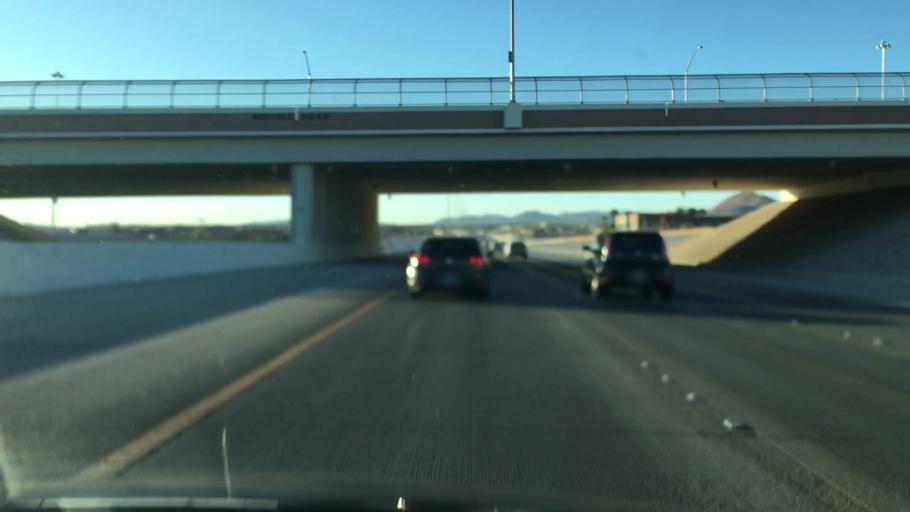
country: US
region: Nevada
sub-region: Clark County
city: Spring Valley
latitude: 36.0856
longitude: -115.2890
